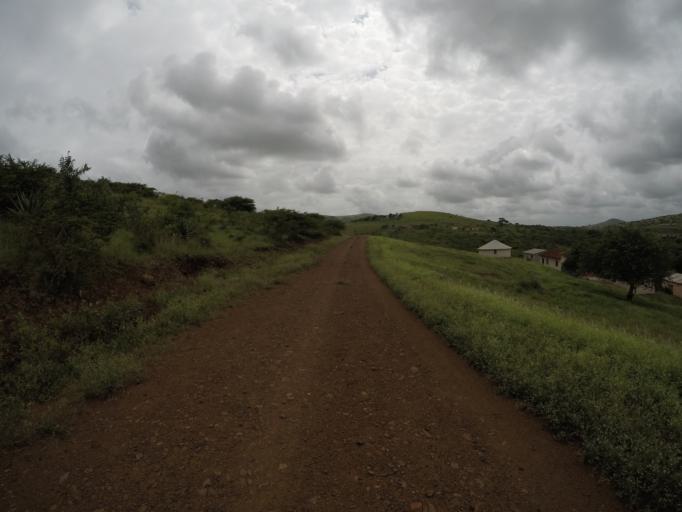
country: ZA
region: KwaZulu-Natal
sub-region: uThungulu District Municipality
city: Empangeni
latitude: -28.6231
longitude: 31.8905
